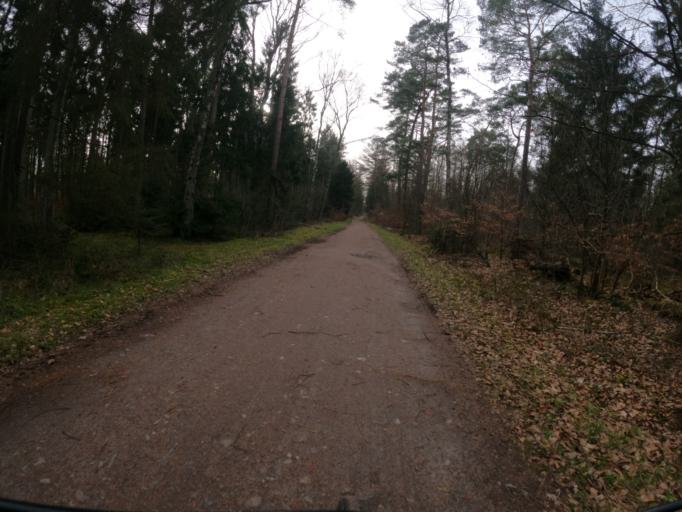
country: DE
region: Schleswig-Holstein
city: Appen
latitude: 53.6131
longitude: 9.7493
